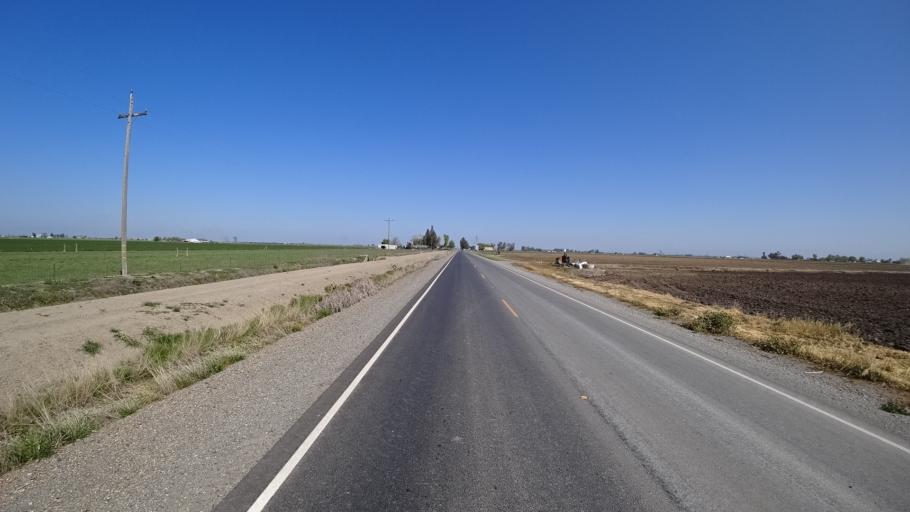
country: US
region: California
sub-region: Glenn County
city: Willows
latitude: 39.5753
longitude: -122.0652
